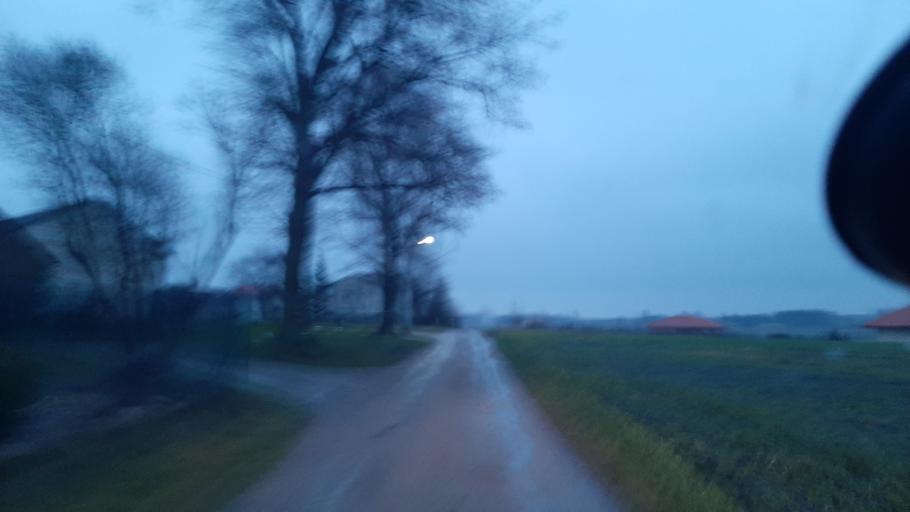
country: PL
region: Lublin Voivodeship
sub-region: Powiat lubelski
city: Jastkow
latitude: 51.3846
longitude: 22.4202
